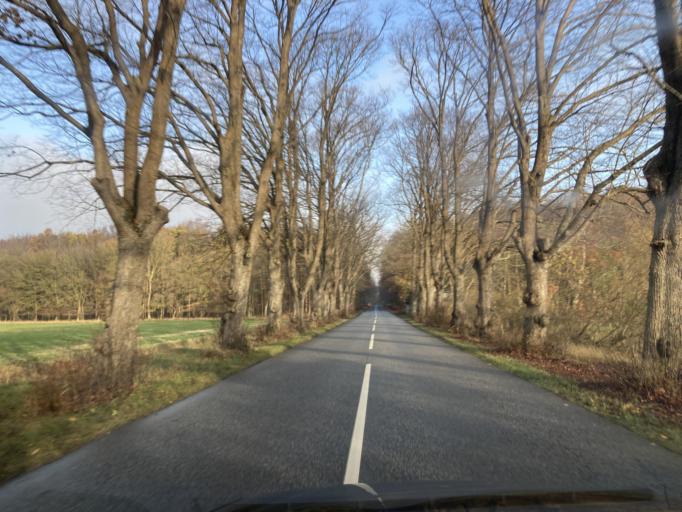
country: DK
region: Zealand
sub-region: Lolland Kommune
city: Rodby
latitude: 54.7629
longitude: 11.3577
